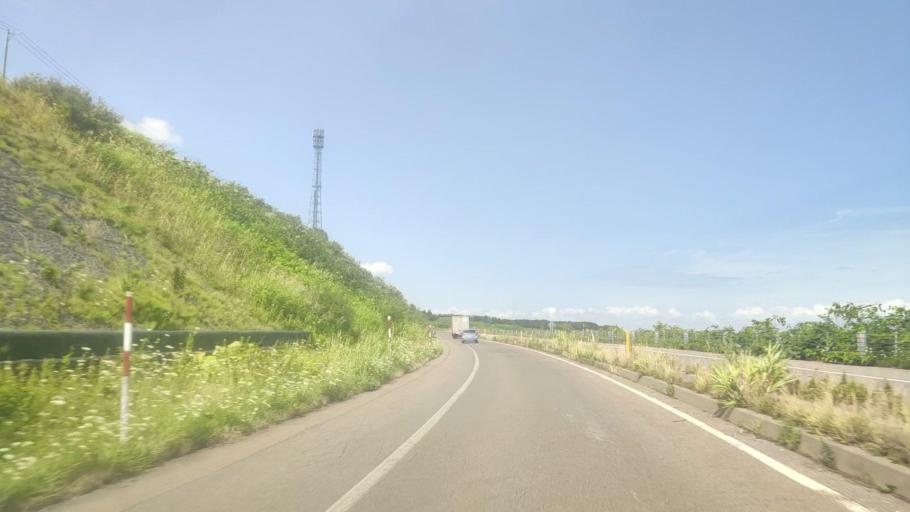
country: JP
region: Hokkaido
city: Nanae
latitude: 42.1984
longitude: 140.4181
